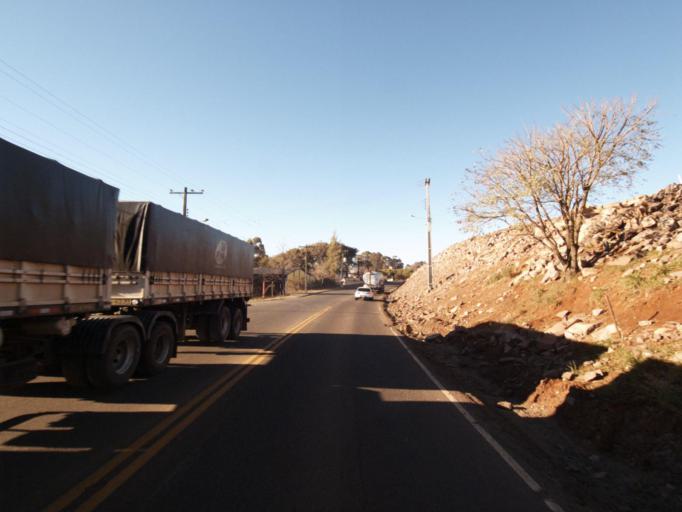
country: AR
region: Misiones
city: Bernardo de Irigoyen
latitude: -26.4523
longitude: -53.5108
